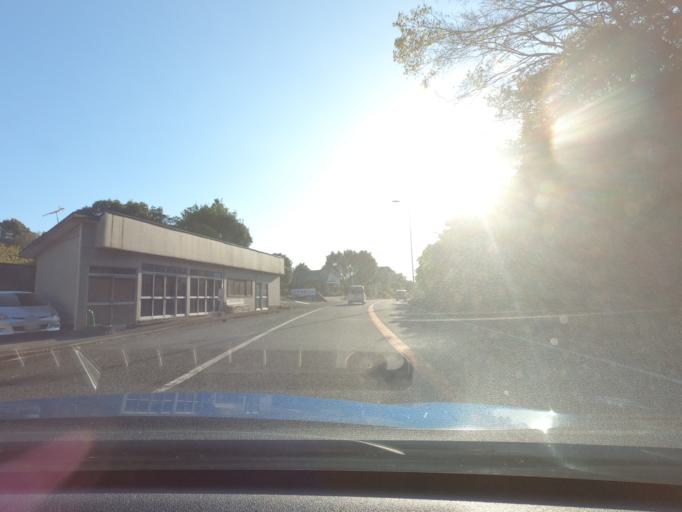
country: JP
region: Kagoshima
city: Akune
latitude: 32.0486
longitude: 130.2205
